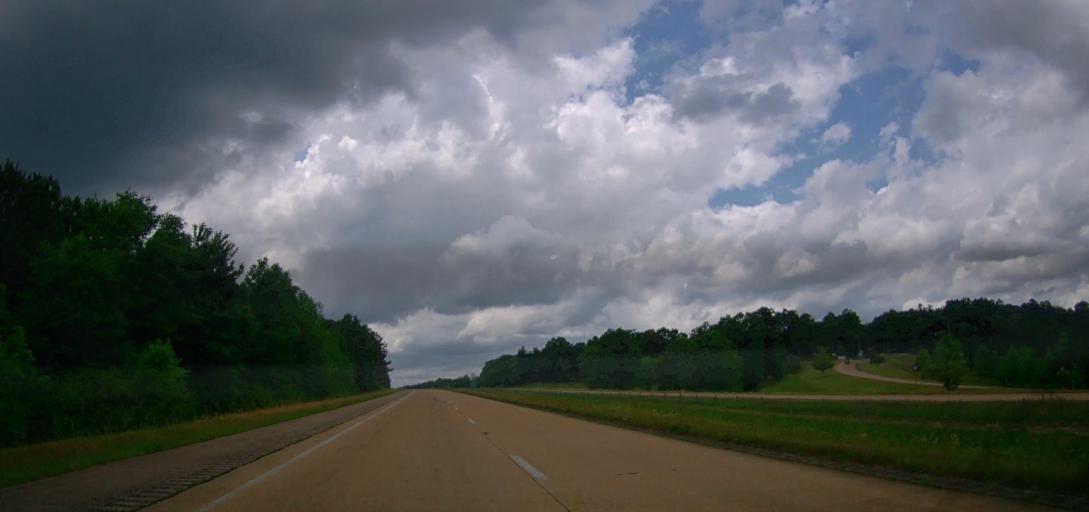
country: US
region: Mississippi
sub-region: Itawamba County
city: Fulton
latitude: 34.2198
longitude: -88.2299
